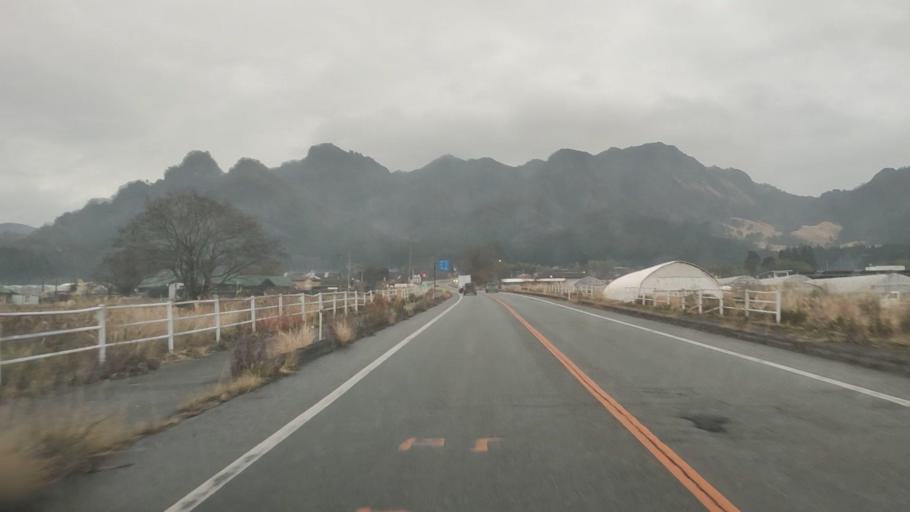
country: JP
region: Kumamoto
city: Aso
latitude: 32.8268
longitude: 131.1264
